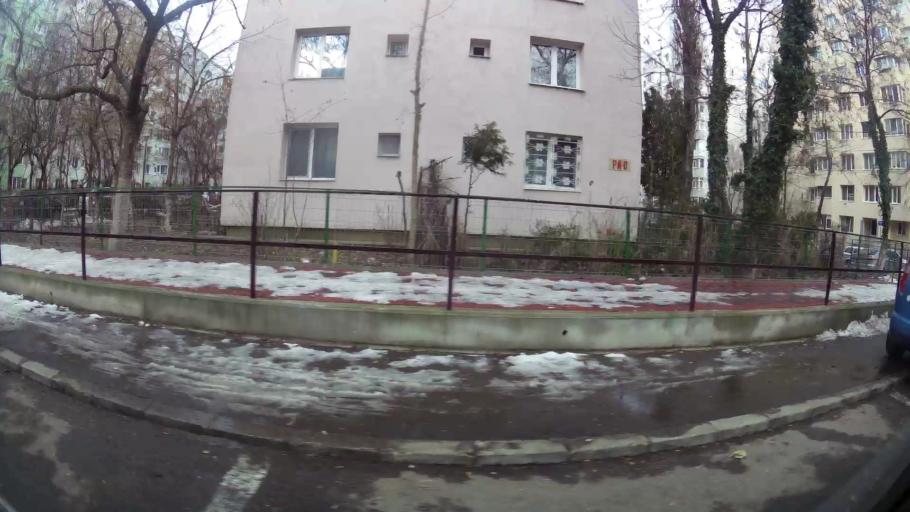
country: RO
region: Ilfov
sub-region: Comuna Popesti-Leordeni
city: Popesti-Leordeni
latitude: 44.4102
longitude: 26.1675
